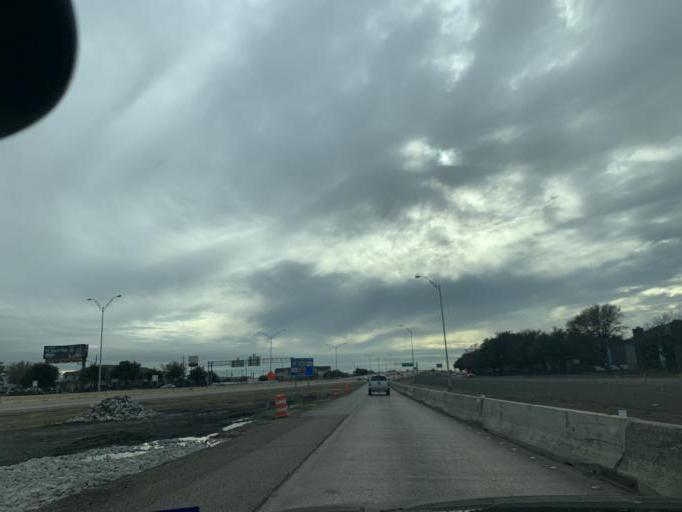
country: US
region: Texas
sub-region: Dallas County
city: Duncanville
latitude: 32.6517
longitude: -96.8812
